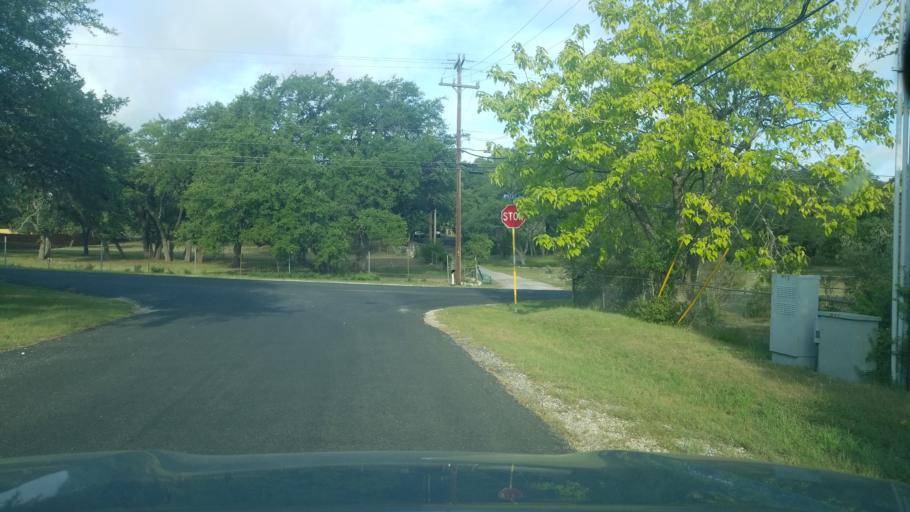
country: US
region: Texas
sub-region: Bexar County
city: Timberwood Park
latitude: 29.7031
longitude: -98.5165
